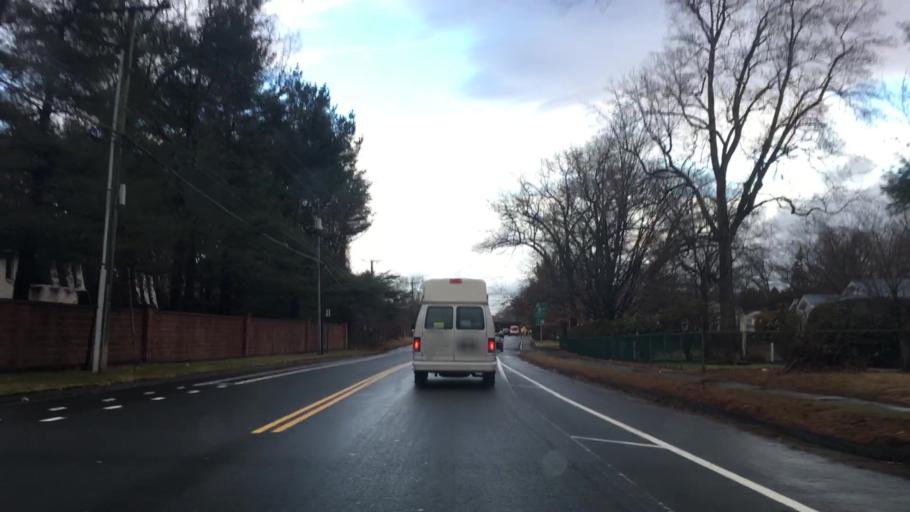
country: US
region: Massachusetts
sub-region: Hampden County
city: Agawam
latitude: 42.0705
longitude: -72.6312
